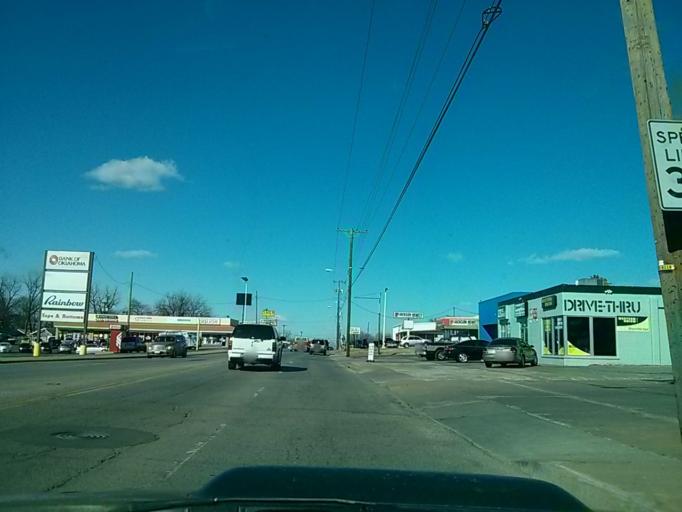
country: US
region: Oklahoma
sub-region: Tulsa County
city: Tulsa
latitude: 36.1785
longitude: -95.9582
